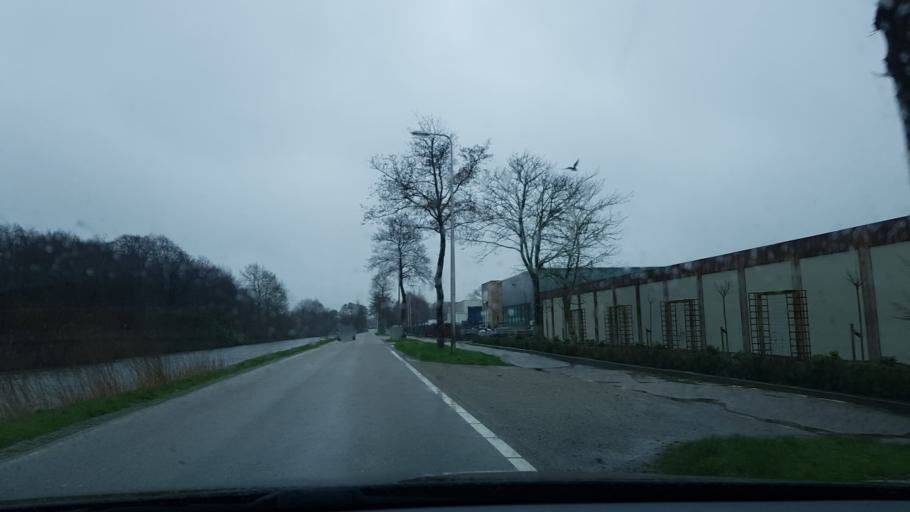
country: NL
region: North Holland
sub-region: Gemeente Bloemendaal
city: Bennebroek
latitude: 52.3316
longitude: 4.5930
